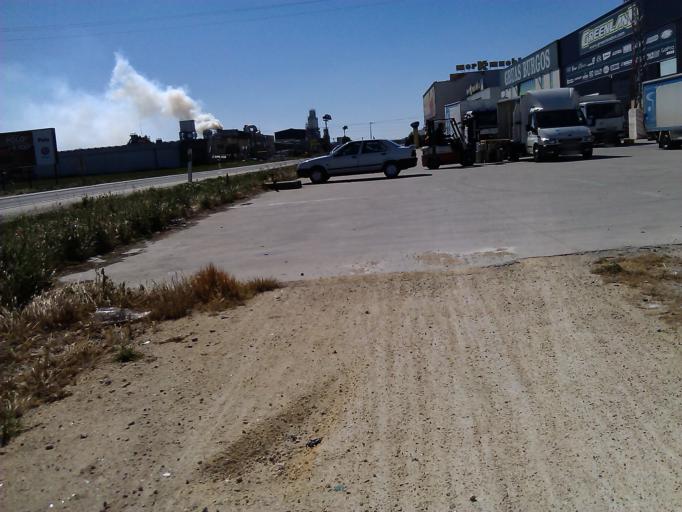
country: ES
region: Castille and Leon
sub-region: Provincia de Burgos
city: Cardenajimeno
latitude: 42.3422
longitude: -3.6157
